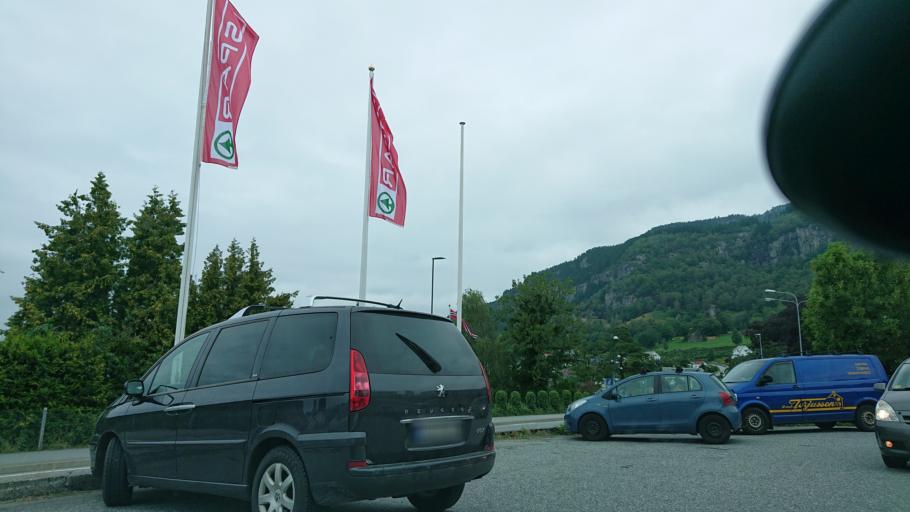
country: NO
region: Rogaland
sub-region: Hjelmeland
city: Hjelmelandsvagen
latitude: 59.2346
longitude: 6.1784
